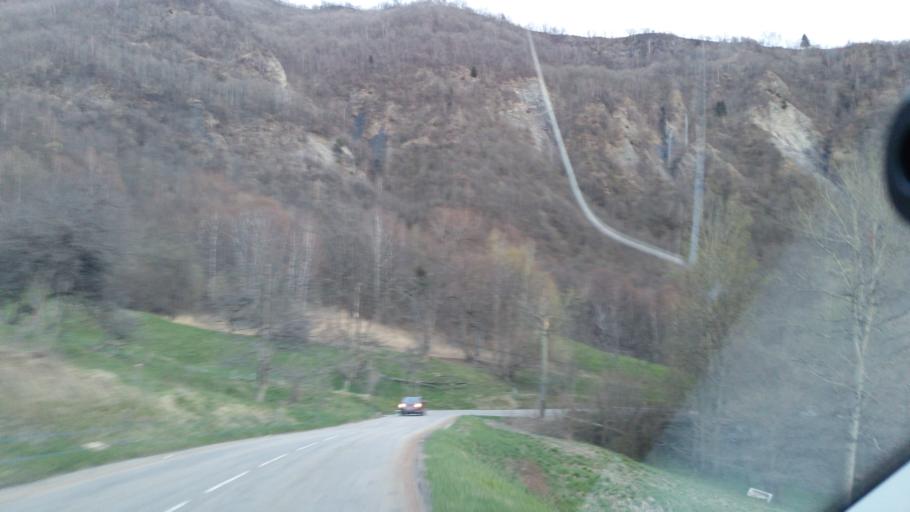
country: FR
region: Rhone-Alpes
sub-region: Departement de la Savoie
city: La Chambre
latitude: 45.3843
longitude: 6.3282
